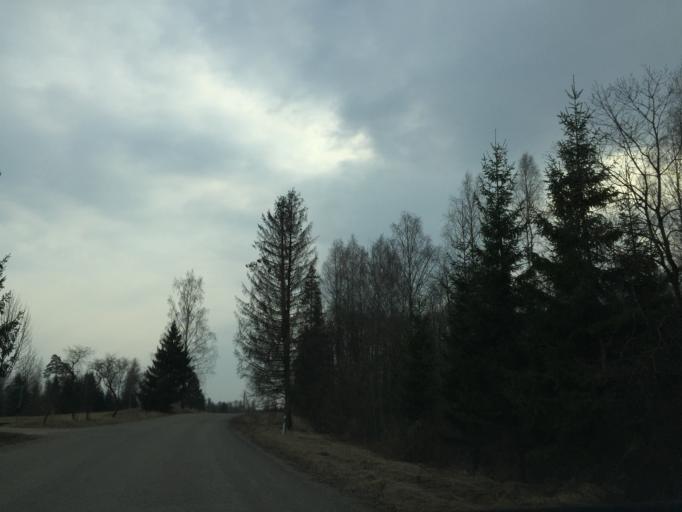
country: LV
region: Priekuli
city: Priekuli
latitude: 57.2289
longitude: 25.3774
